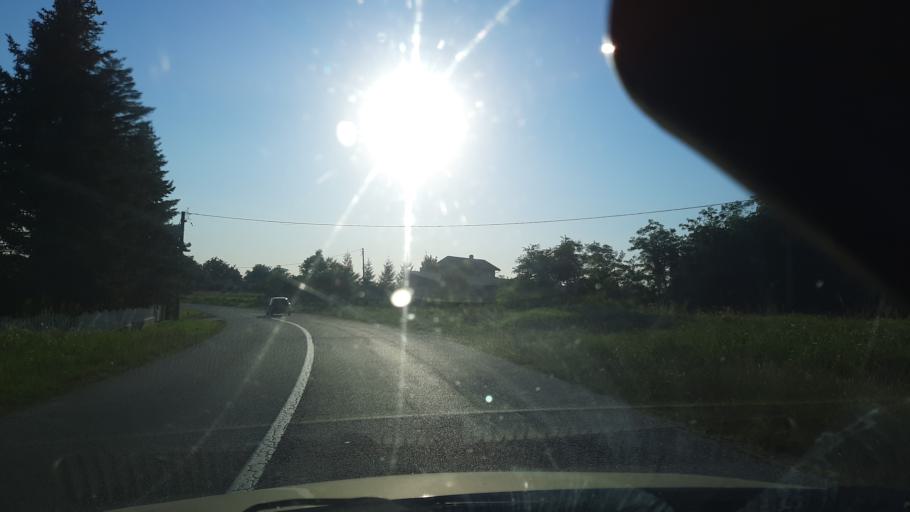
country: RS
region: Central Serbia
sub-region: Branicevski Okrug
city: Malo Crnice
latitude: 44.5859
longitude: 21.4073
